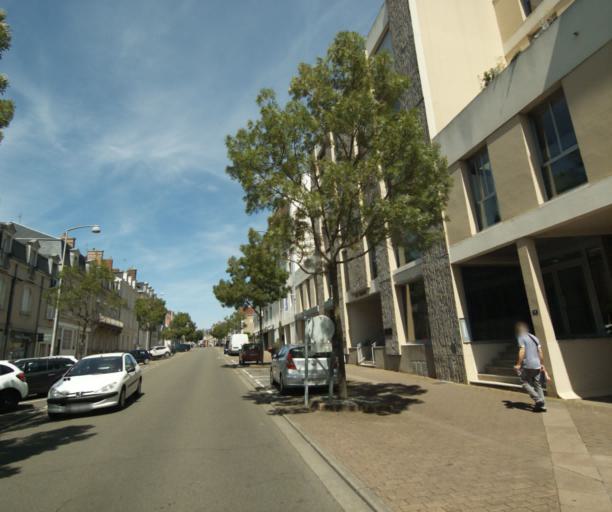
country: FR
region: Pays de la Loire
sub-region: Departement de la Mayenne
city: Laval
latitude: 48.0717
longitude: -0.7649
